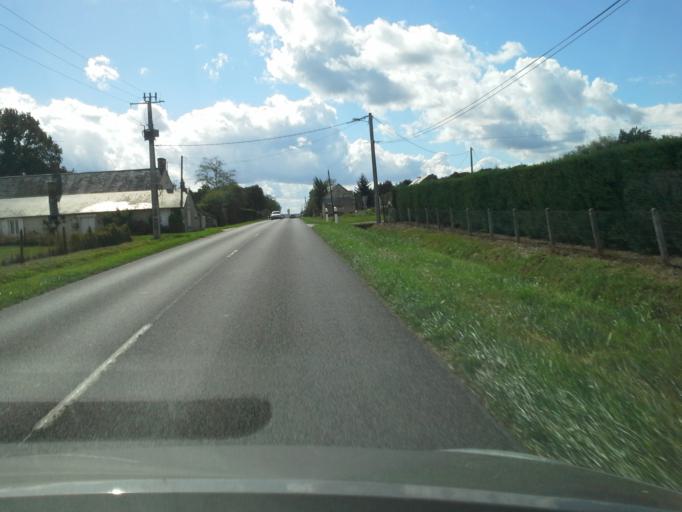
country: FR
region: Centre
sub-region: Departement du Loir-et-Cher
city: Pontlevoy
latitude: 47.4175
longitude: 1.2770
